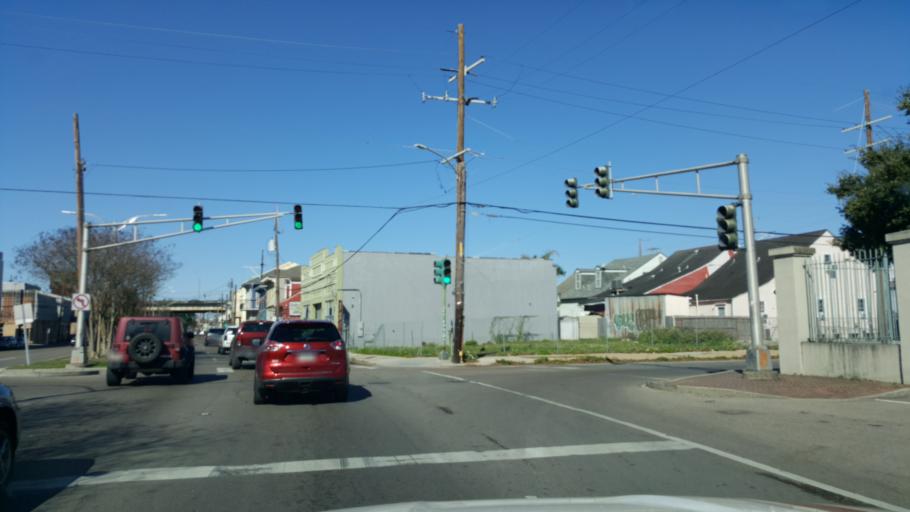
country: US
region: Louisiana
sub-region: Orleans Parish
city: New Orleans
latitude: 29.9630
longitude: -90.0712
